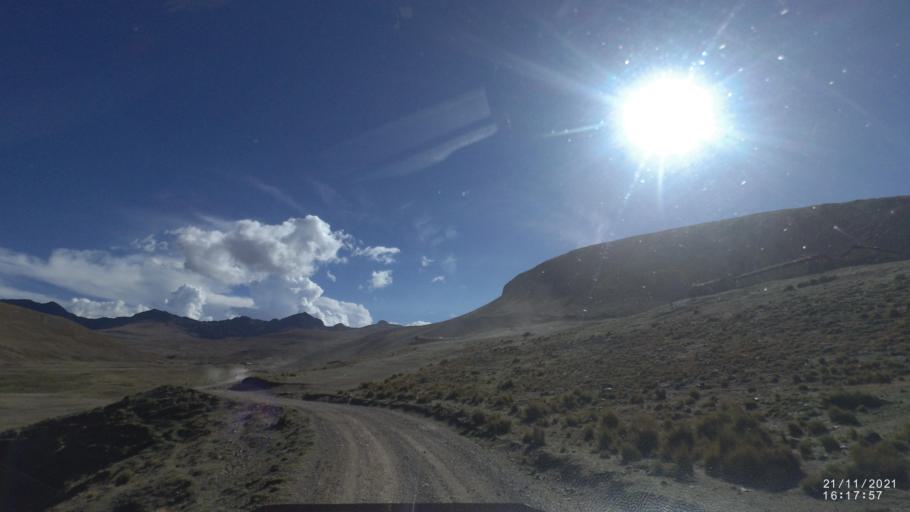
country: BO
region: Cochabamba
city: Cochabamba
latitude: -17.0047
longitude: -66.2825
